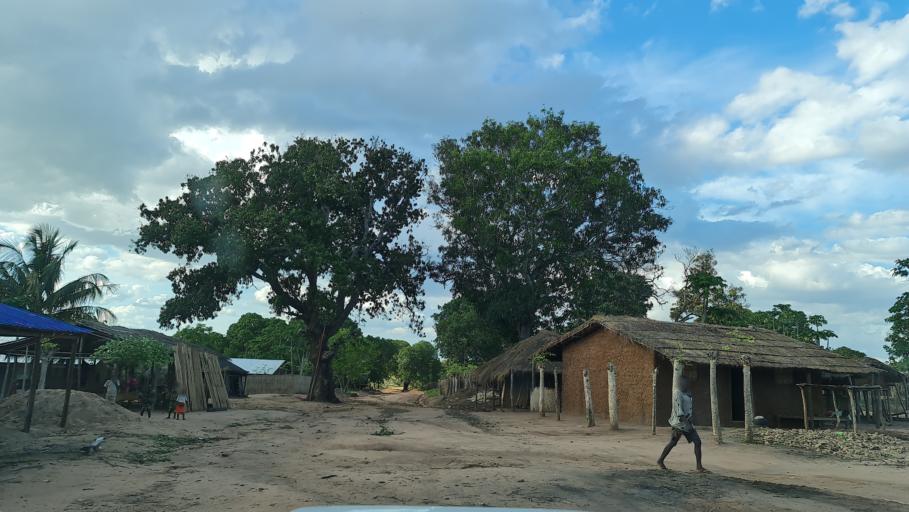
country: MZ
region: Cabo Delgado
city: Pemba
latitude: -13.5547
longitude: 40.1038
